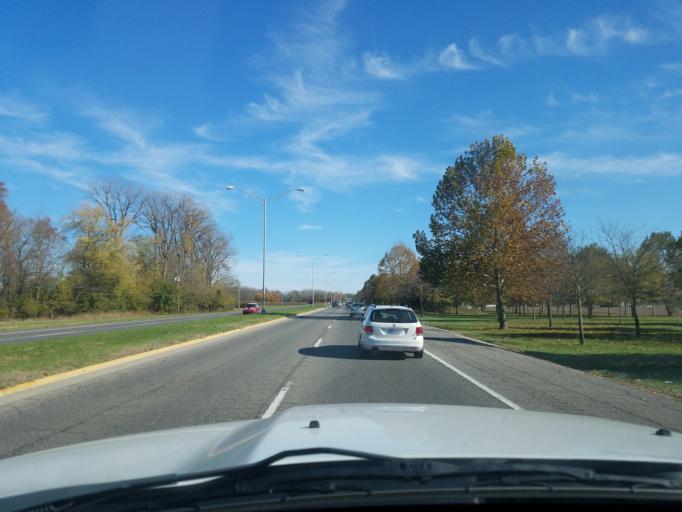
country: US
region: Indiana
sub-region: Bartholomew County
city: Columbus
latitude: 39.1999
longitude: -85.9428
